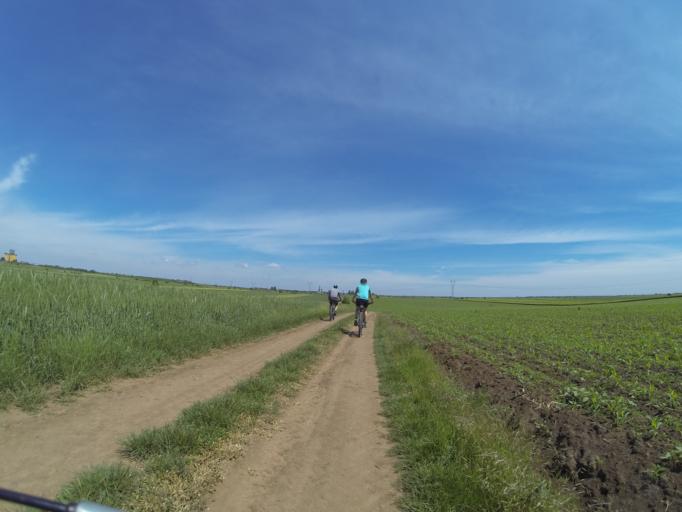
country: RO
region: Dolj
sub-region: Comuna Leu
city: Leu
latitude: 44.1875
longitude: 24.0449
